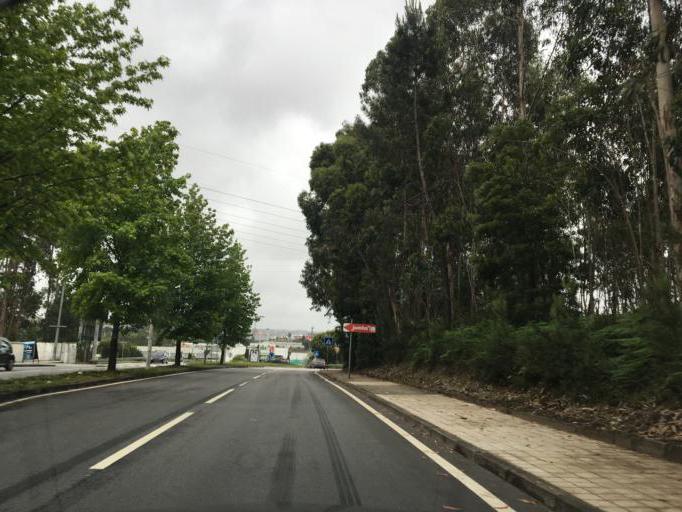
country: PT
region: Porto
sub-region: Maia
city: Maia
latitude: 41.2464
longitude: -8.6233
